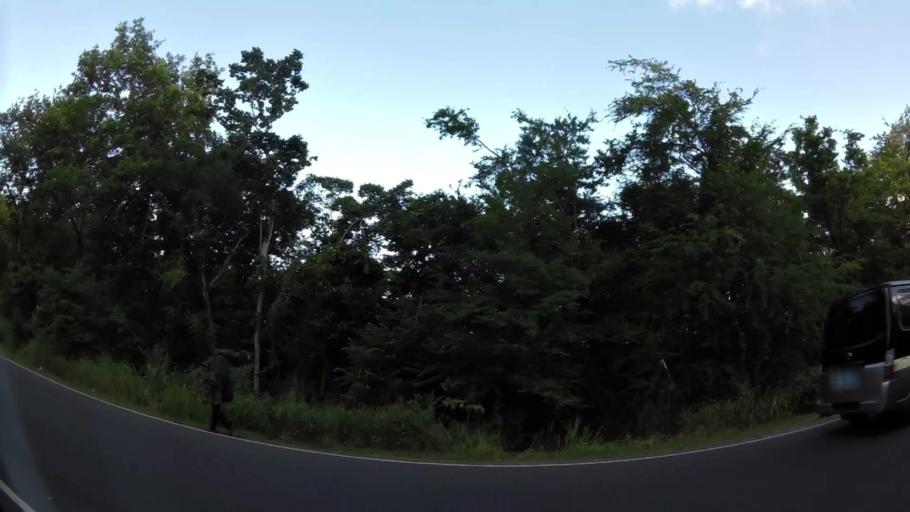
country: LC
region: Castries Quarter
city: Bisee
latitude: 14.0421
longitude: -60.9691
